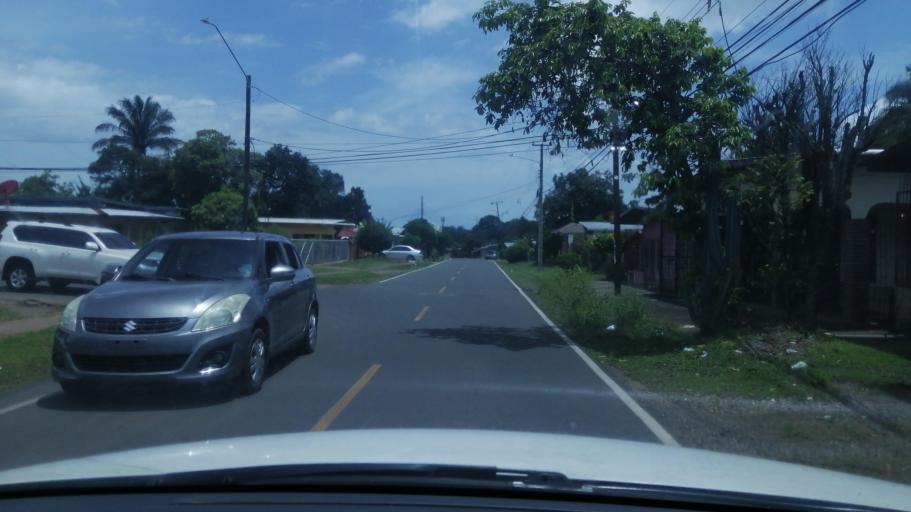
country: PA
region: Chiriqui
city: David
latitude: 8.4168
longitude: -82.4270
